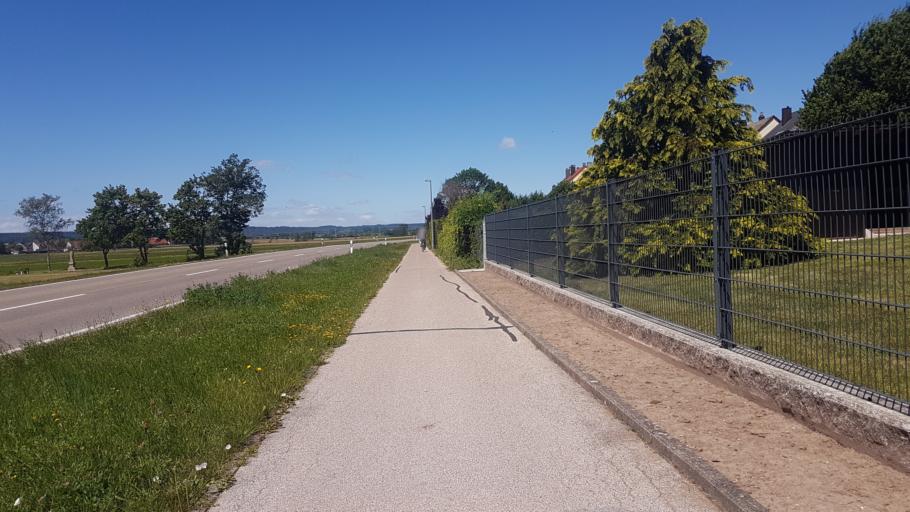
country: DE
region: Bavaria
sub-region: Regierungsbezirk Mittelfranken
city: Herrieden
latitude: 49.2354
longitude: 10.4879
